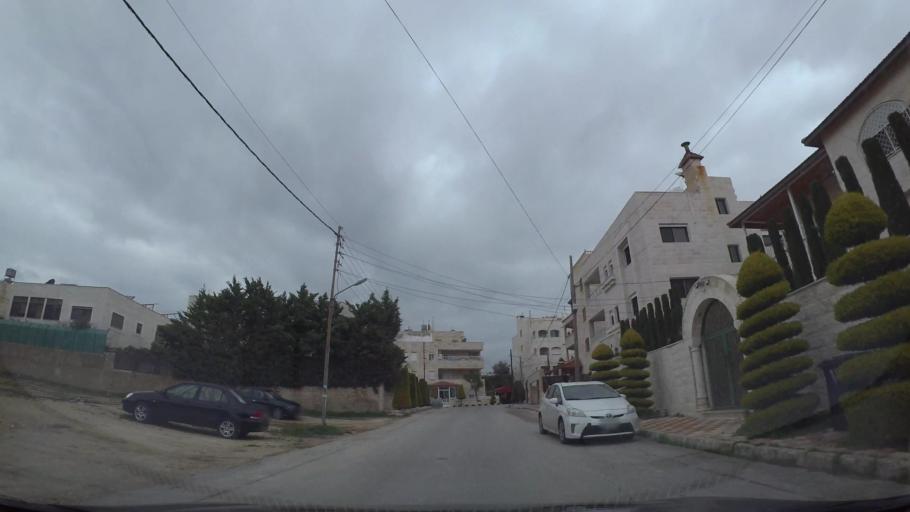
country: JO
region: Amman
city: Wadi as Sir
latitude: 31.9672
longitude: 35.8336
